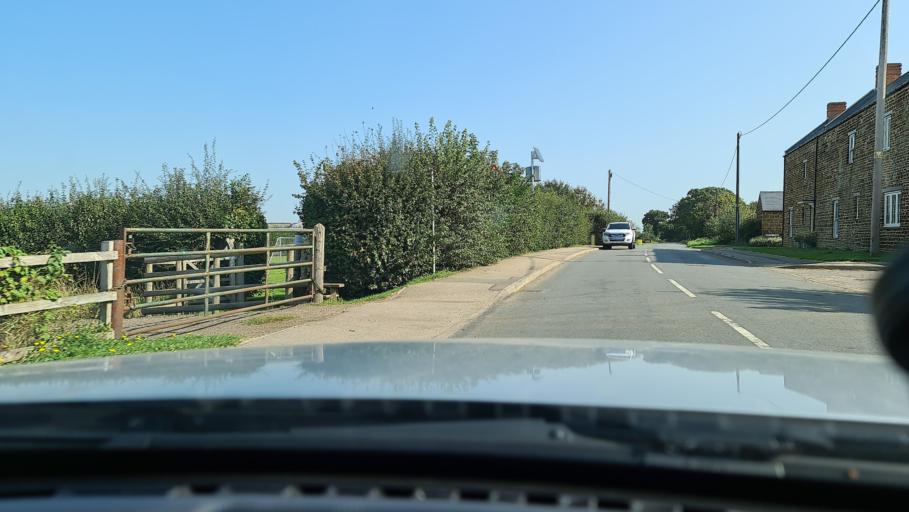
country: GB
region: England
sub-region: Northamptonshire
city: Bugbrooke
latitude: 52.1841
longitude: -1.0735
